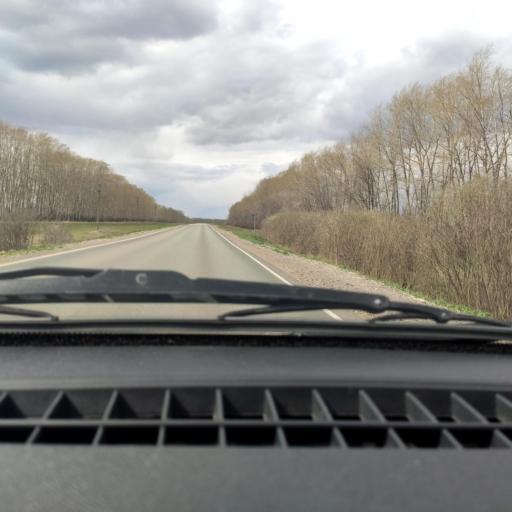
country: RU
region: Bashkortostan
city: Alekseyevka
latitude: 55.0605
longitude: 55.1066
